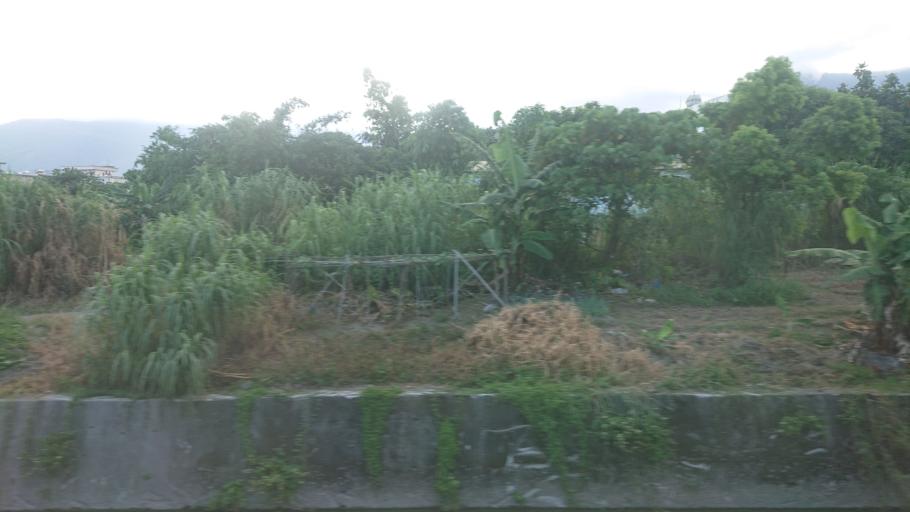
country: TW
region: Taiwan
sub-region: Hualien
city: Hualian
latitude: 23.9802
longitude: 121.5947
